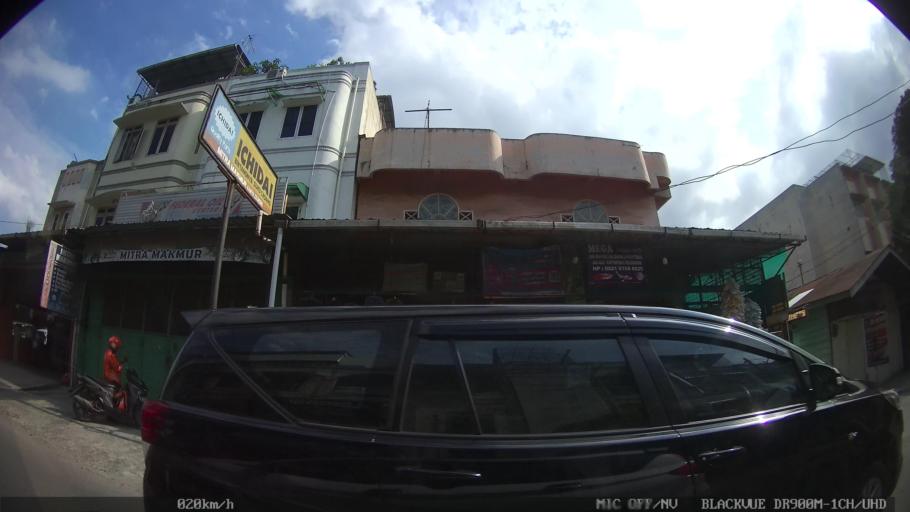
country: ID
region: North Sumatra
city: Medan
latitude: 3.6203
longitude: 98.6676
